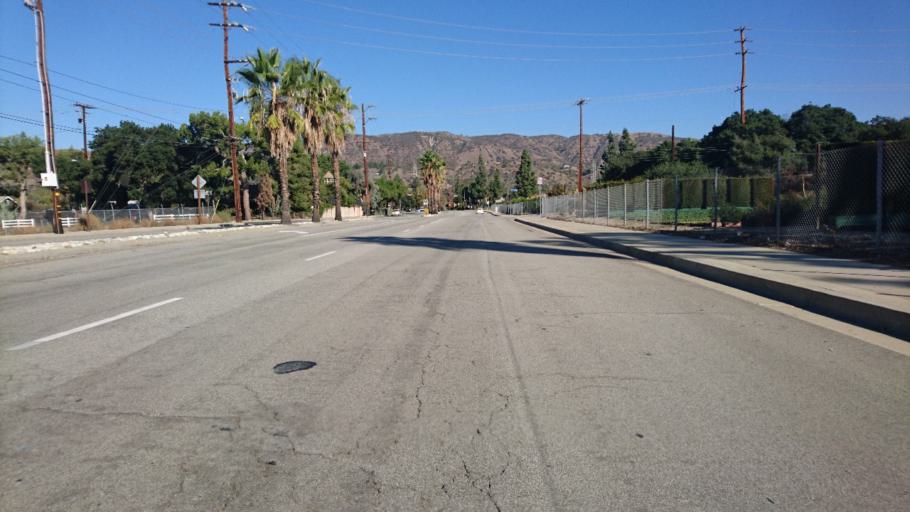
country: US
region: California
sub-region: Los Angeles County
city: San Dimas
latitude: 34.1205
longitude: -117.7939
